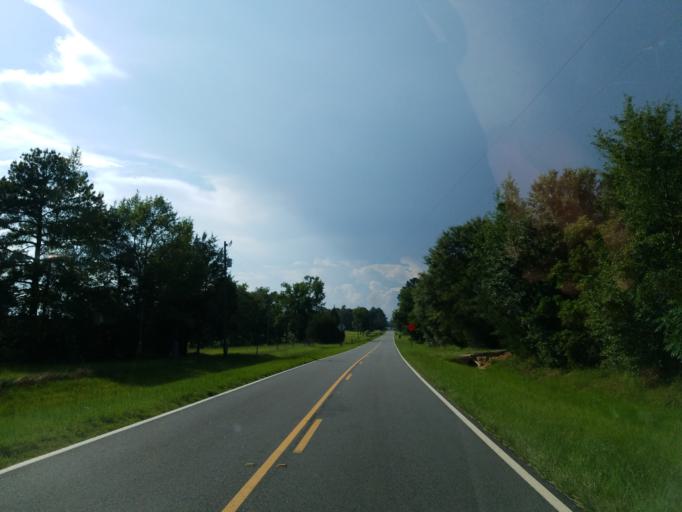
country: US
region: Georgia
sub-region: Lowndes County
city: Hahira
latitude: 31.0210
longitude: -83.4351
